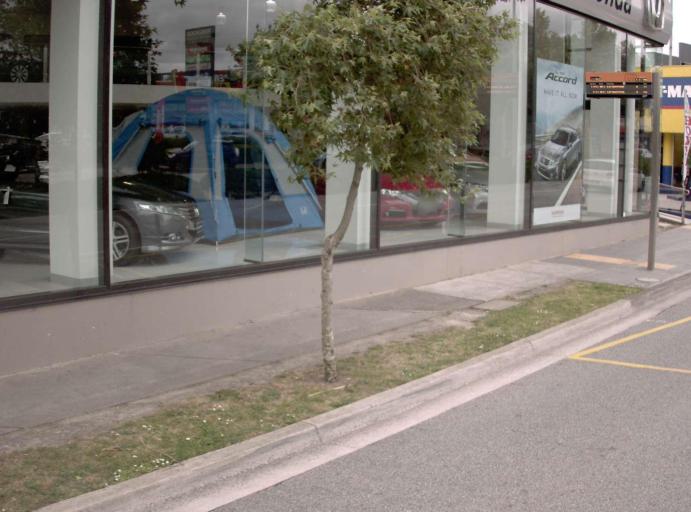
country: AU
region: Victoria
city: Mitcham
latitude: -37.8169
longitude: 145.2231
